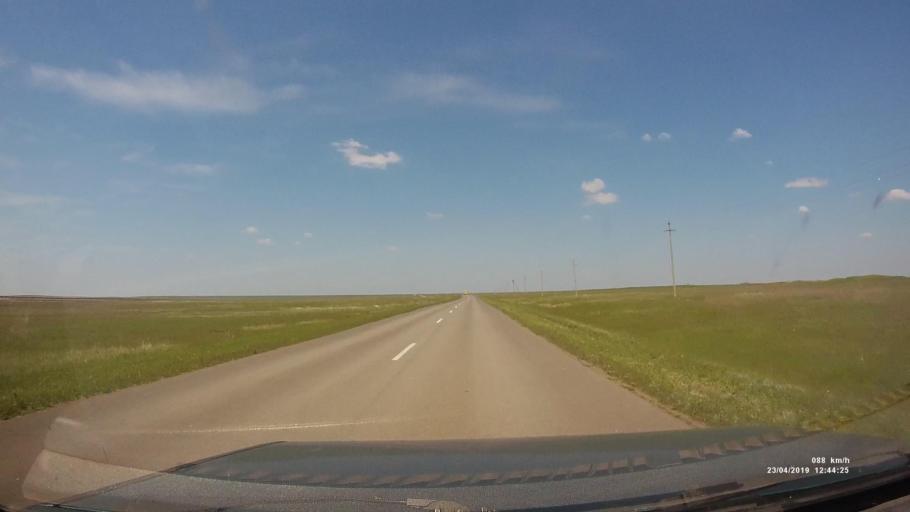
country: RU
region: Kalmykiya
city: Yashalta
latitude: 46.4766
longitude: 42.6475
